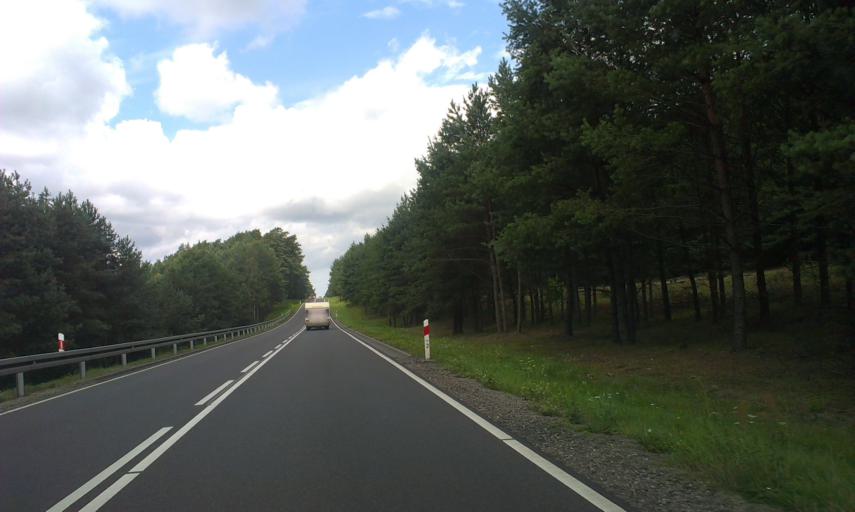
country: PL
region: West Pomeranian Voivodeship
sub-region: Powiat koszalinski
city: Sianow
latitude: 54.1076
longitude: 16.3359
